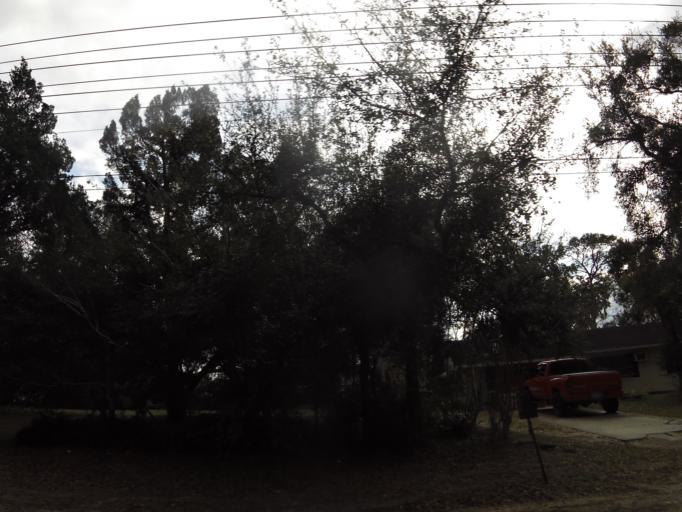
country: US
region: Florida
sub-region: Volusia County
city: Orange City
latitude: 28.9486
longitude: -81.2794
